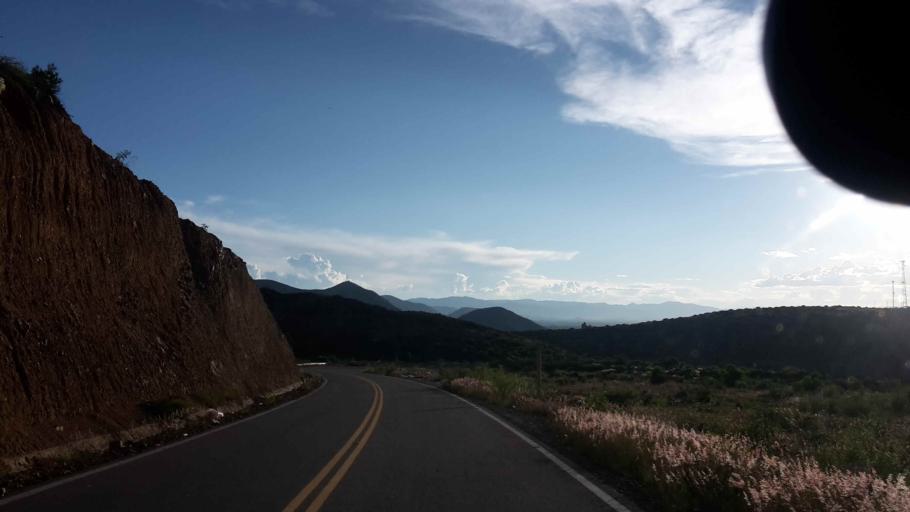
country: BO
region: Cochabamba
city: Arani
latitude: -17.5828
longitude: -65.7545
